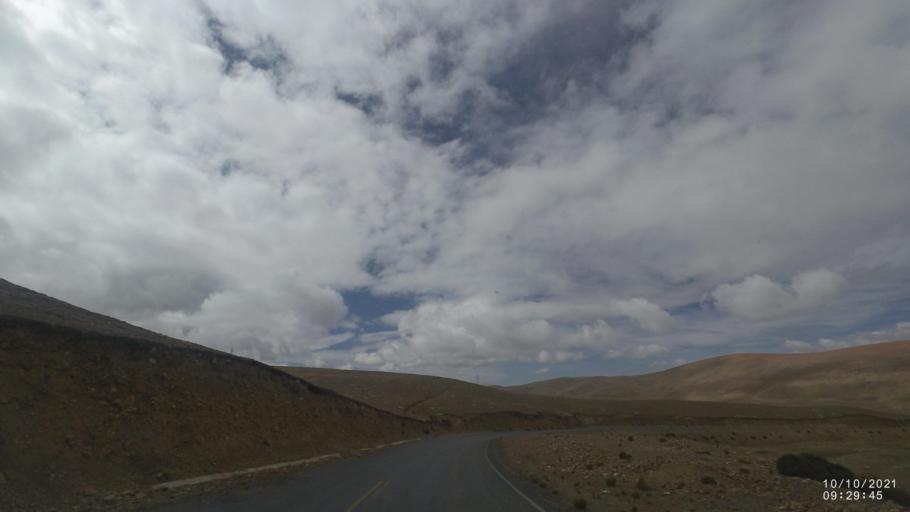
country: BO
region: La Paz
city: Quime
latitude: -17.1163
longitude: -67.3259
